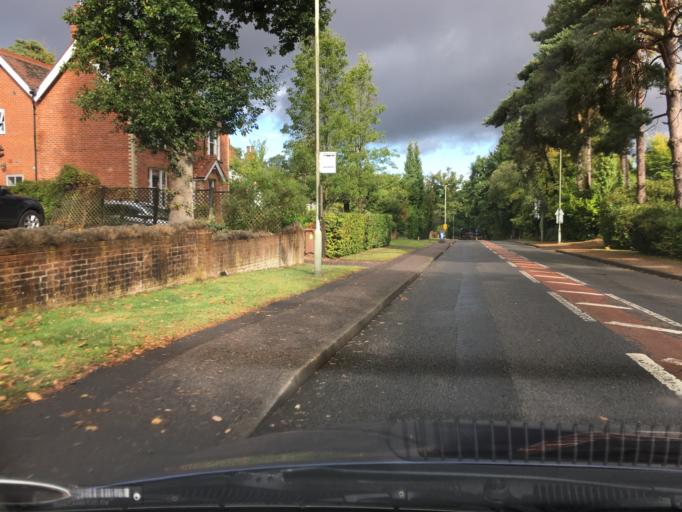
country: GB
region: England
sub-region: Bracknell Forest
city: Crowthorne
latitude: 51.3746
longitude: -0.8041
